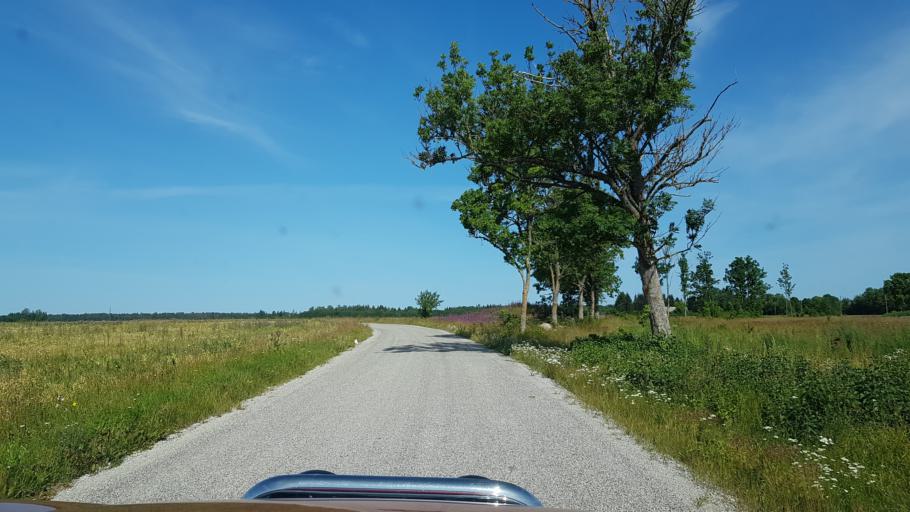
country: EE
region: Jaervamaa
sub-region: Jaerva-Jaani vald
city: Jarva-Jaani
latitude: 59.0868
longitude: 25.7522
